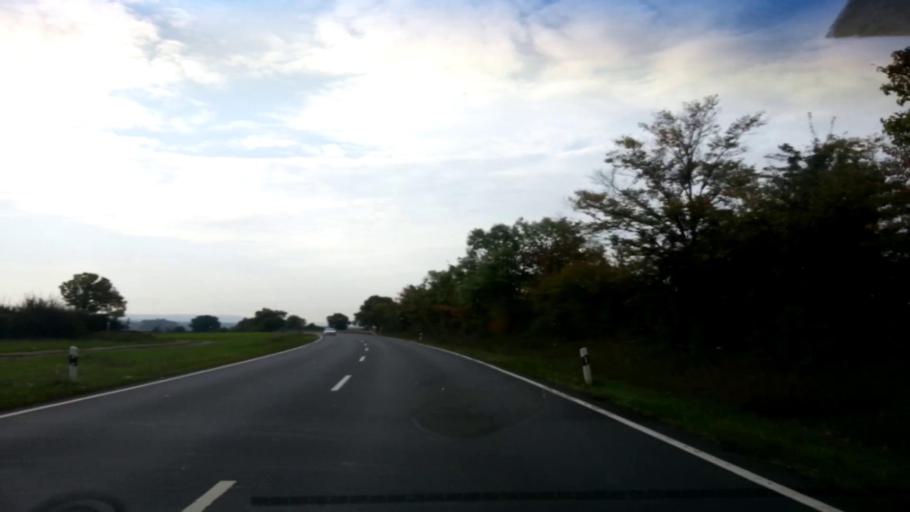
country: DE
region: Bavaria
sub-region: Regierungsbezirk Unterfranken
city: Lulsfeld
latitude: 49.8600
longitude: 10.3501
